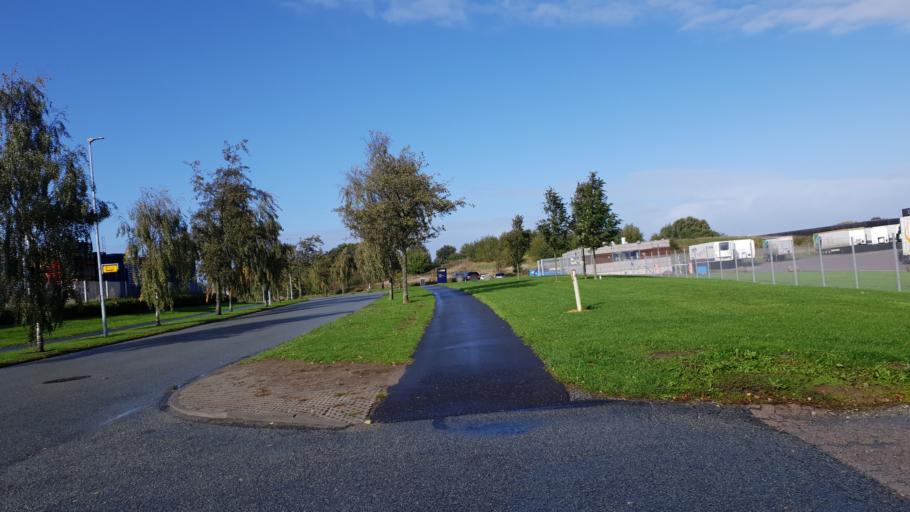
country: DK
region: South Denmark
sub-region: Kolding Kommune
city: Kolding
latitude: 55.5350
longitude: 9.4781
